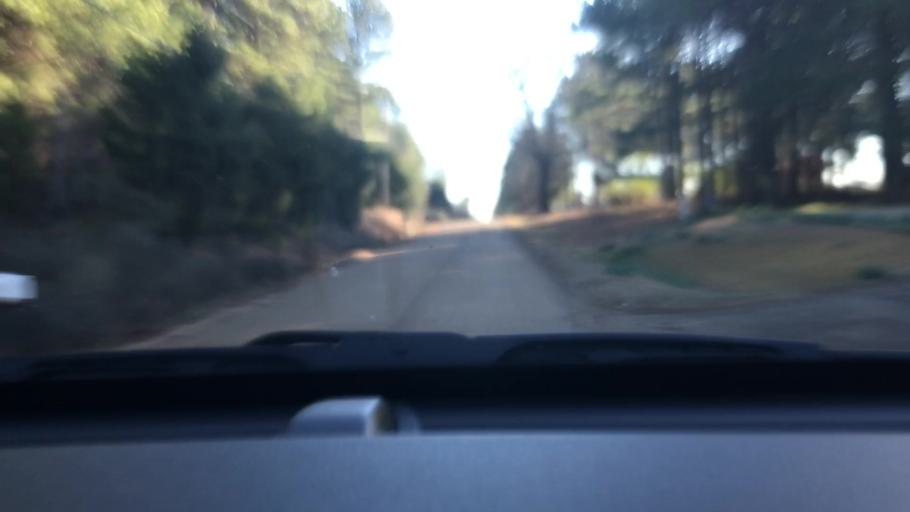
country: US
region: Arkansas
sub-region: Hempstead County
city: Hope
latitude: 33.6388
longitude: -93.5718
